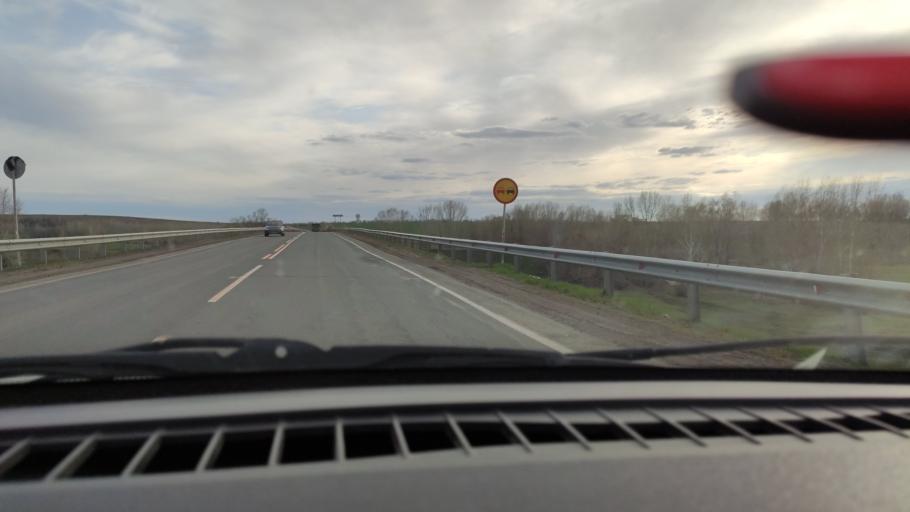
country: RU
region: Orenburg
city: Sakmara
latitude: 52.1957
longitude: 55.3066
